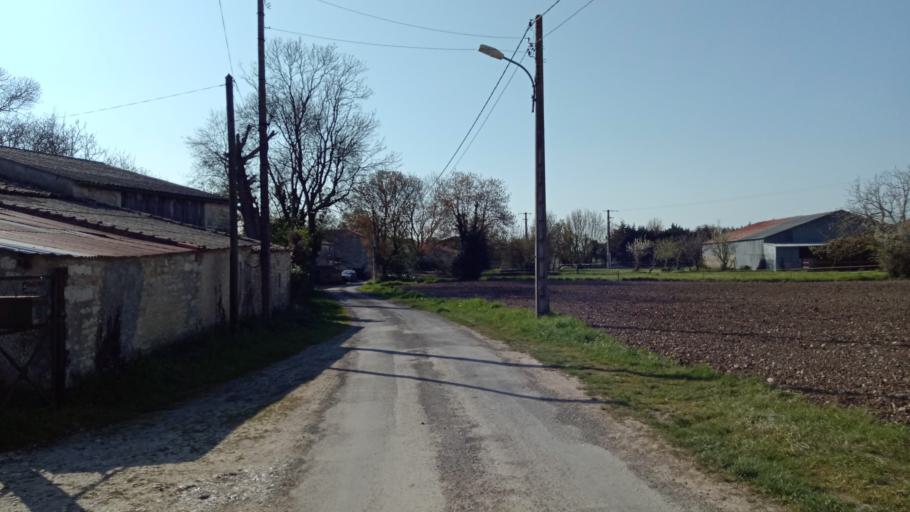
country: FR
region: Poitou-Charentes
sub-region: Departement de la Charente-Maritime
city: Verines
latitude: 46.1651
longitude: -0.9463
